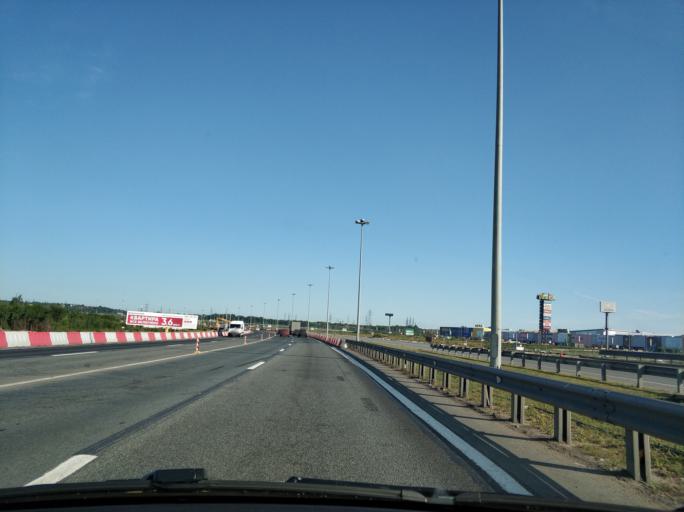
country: RU
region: Leningrad
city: Bugry
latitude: 60.0850
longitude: 30.3776
